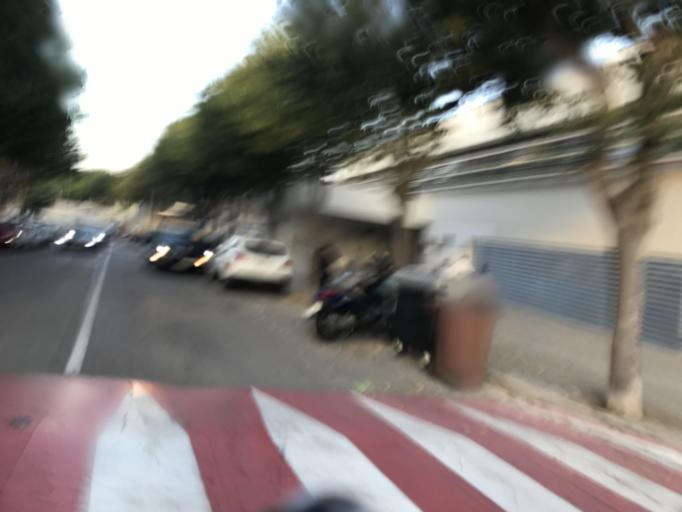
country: ES
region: Catalonia
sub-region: Provincia de Barcelona
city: Parets del Valles
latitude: 41.5614
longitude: 2.2216
